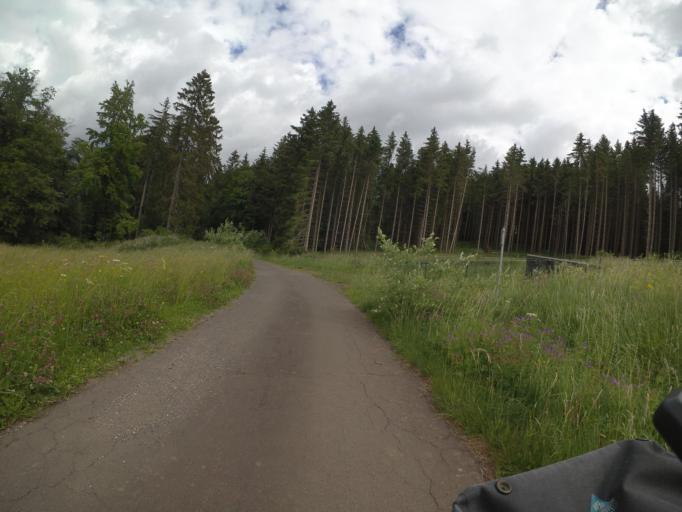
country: DE
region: Rheinland-Pfalz
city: Hinterweiler
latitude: 50.2335
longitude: 6.7621
